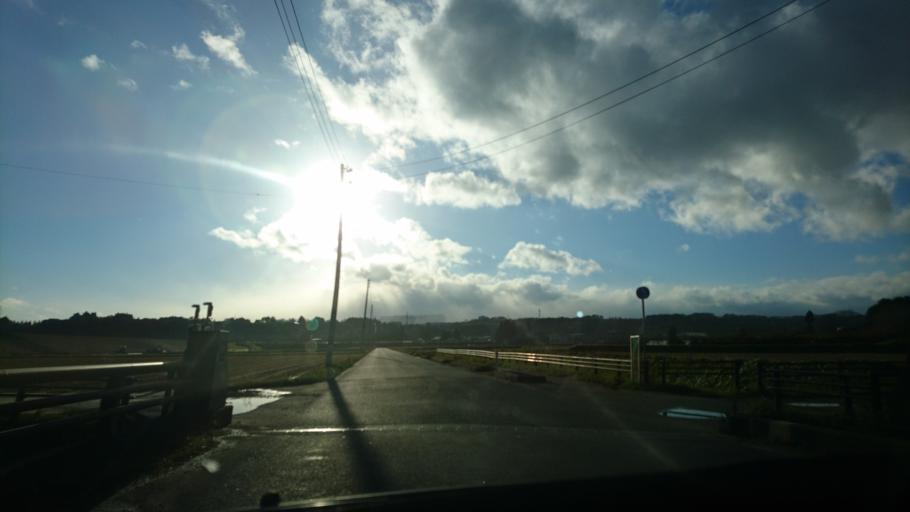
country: JP
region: Iwate
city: Mizusawa
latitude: 39.0365
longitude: 141.1290
